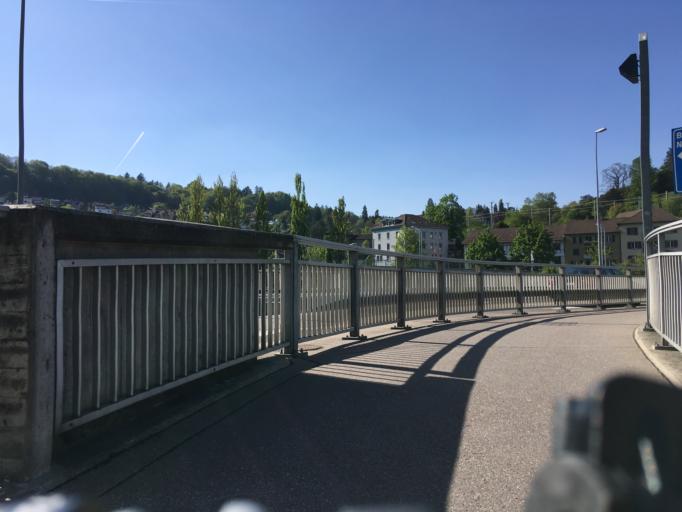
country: CH
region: Zurich
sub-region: Bezirk Andelfingen
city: Flurlingen
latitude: 47.6921
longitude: 8.6269
